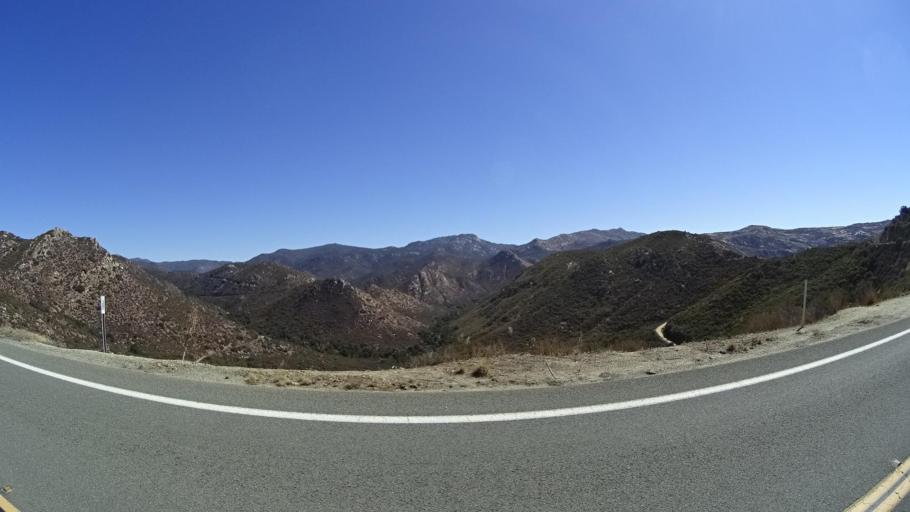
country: US
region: California
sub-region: San Diego County
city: Descanso
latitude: 32.7516
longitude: -116.6712
